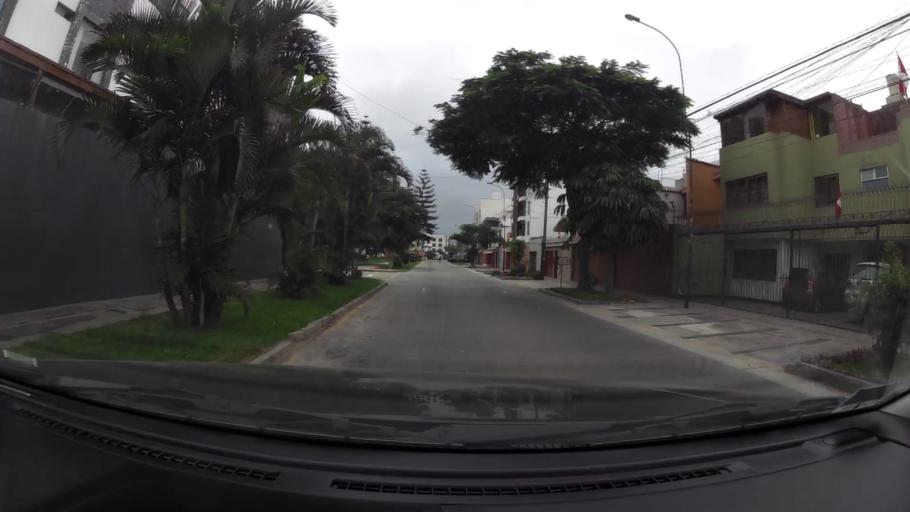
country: PE
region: Lima
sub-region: Lima
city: Surco
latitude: -12.1423
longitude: -76.9992
